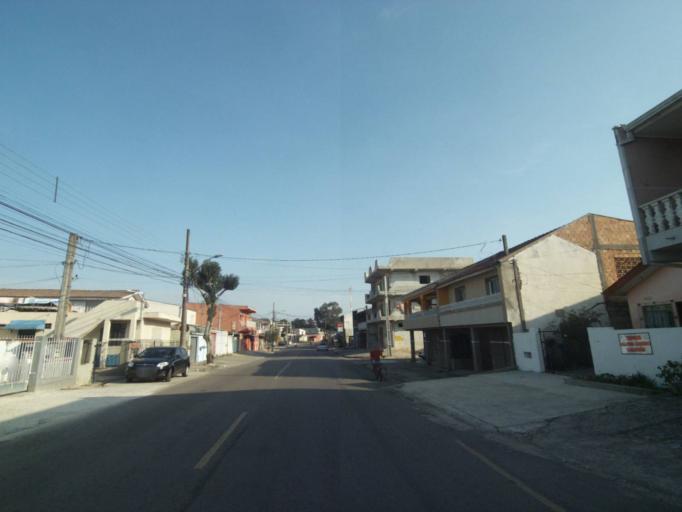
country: BR
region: Parana
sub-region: Curitiba
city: Curitiba
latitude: -25.4883
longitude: -49.3357
